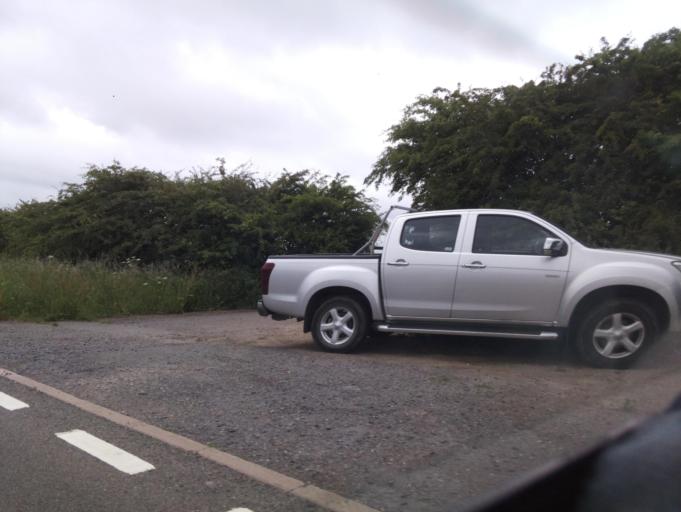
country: GB
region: England
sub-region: Leicestershire
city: Houghton on the Hill
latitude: 52.6212
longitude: -0.9478
